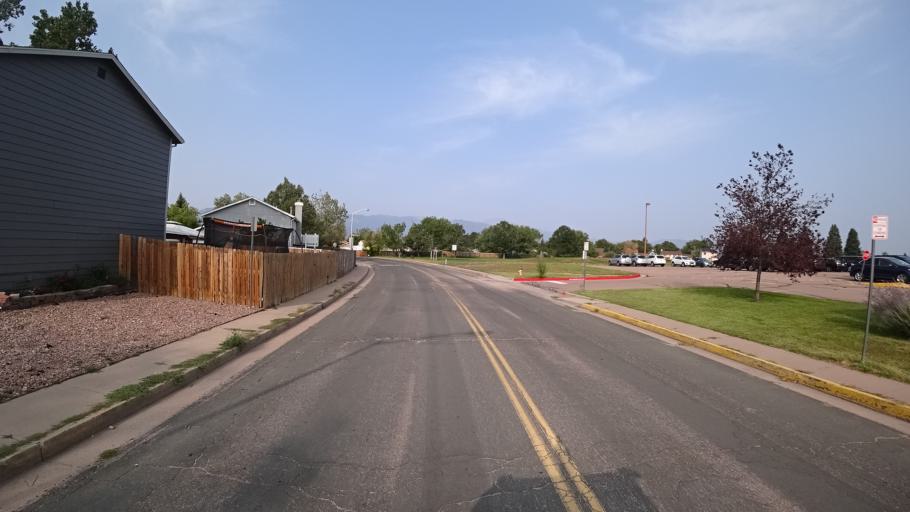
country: US
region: Colorado
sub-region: El Paso County
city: Stratmoor
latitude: 38.8003
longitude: -104.7372
